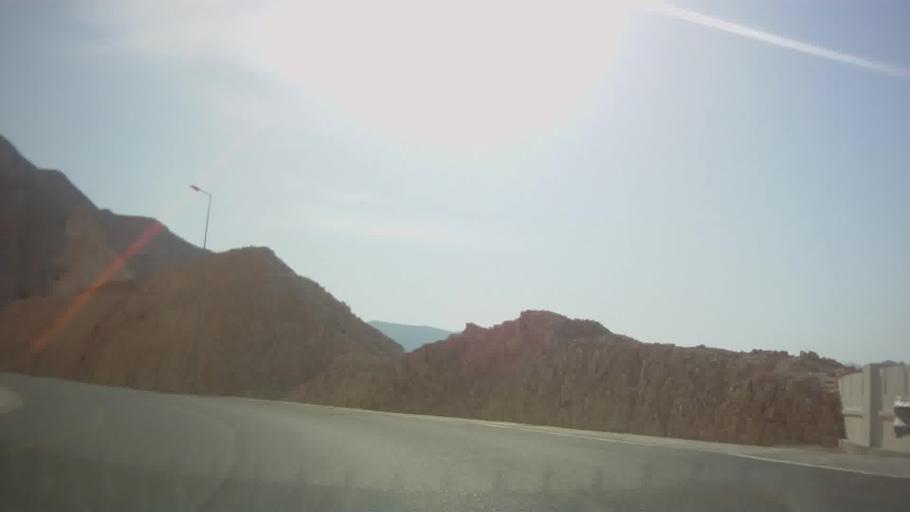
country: OM
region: Muhafazat Masqat
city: Muscat
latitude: 23.5454
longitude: 58.6550
